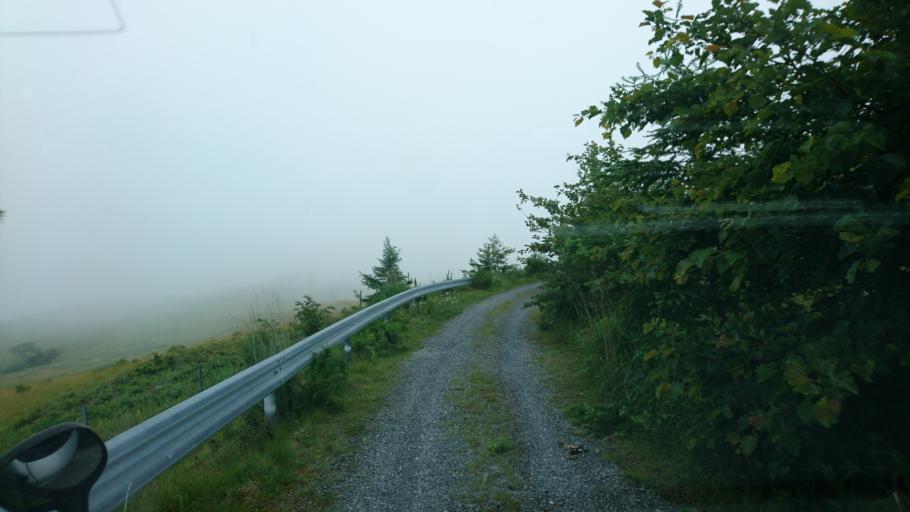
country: JP
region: Iwate
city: Ofunato
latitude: 39.1708
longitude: 141.7881
